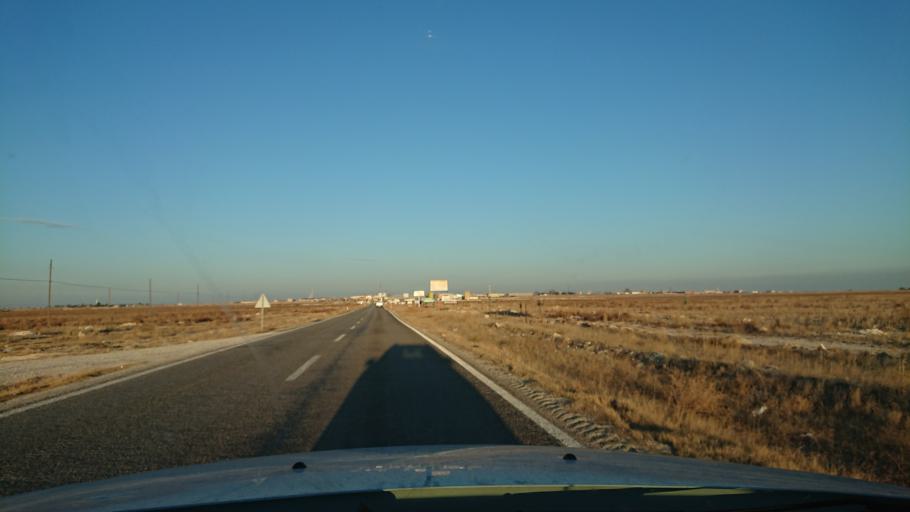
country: TR
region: Aksaray
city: Eskil
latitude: 38.3884
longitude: 33.3843
